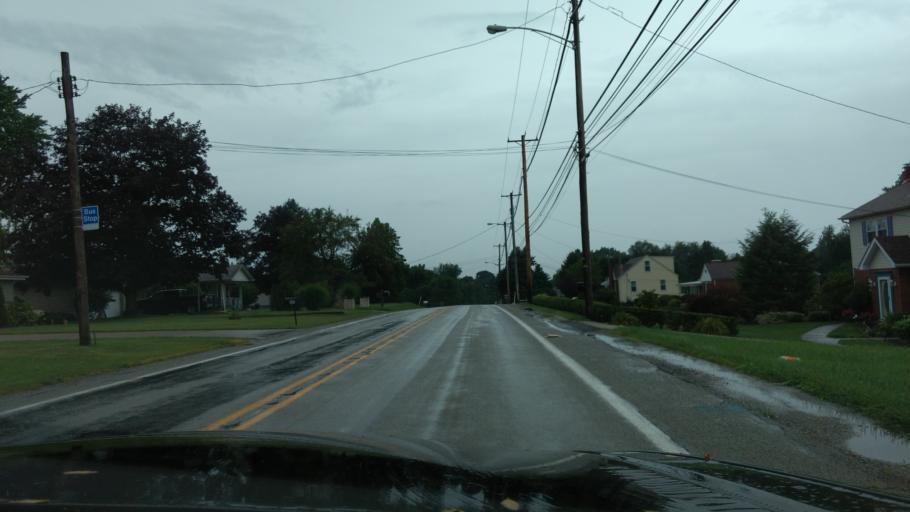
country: US
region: Pennsylvania
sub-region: Allegheny County
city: Emsworth
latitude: 40.5020
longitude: -80.1203
